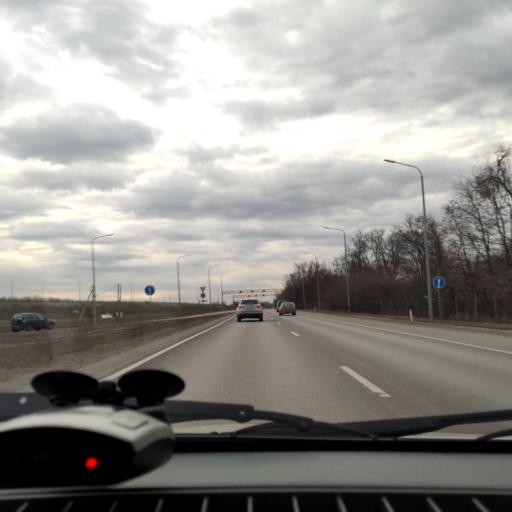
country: RU
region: Voronezj
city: Podgornoye
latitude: 51.8388
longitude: 39.2138
